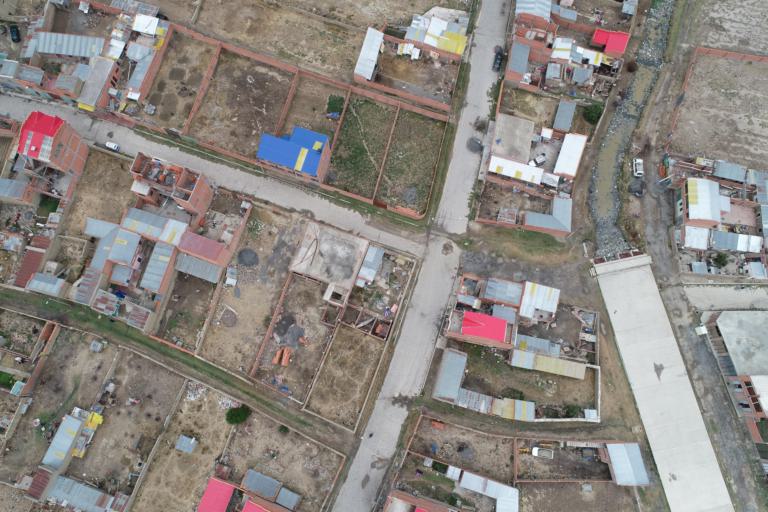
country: BO
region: La Paz
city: Achacachi
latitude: -16.0501
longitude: -68.6834
